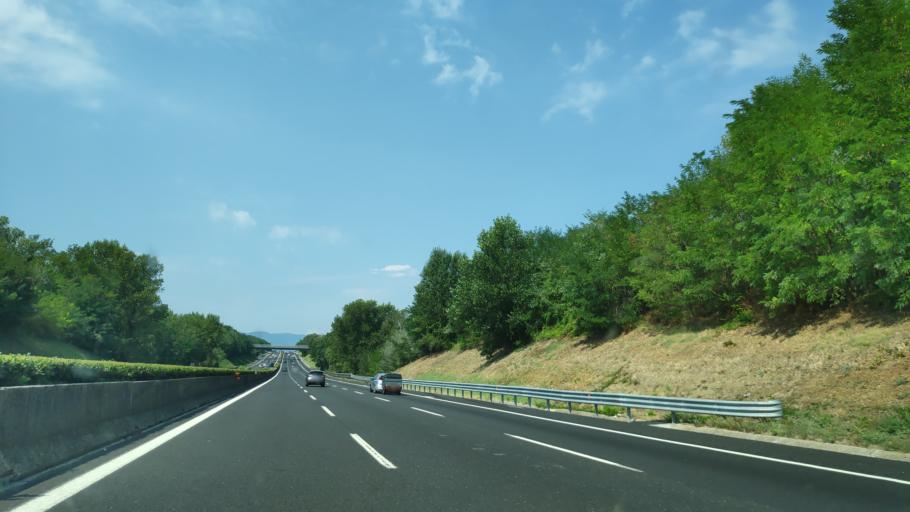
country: IT
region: Latium
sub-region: Provincia di Frosinone
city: Ceprano
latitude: 41.5439
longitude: 13.5466
